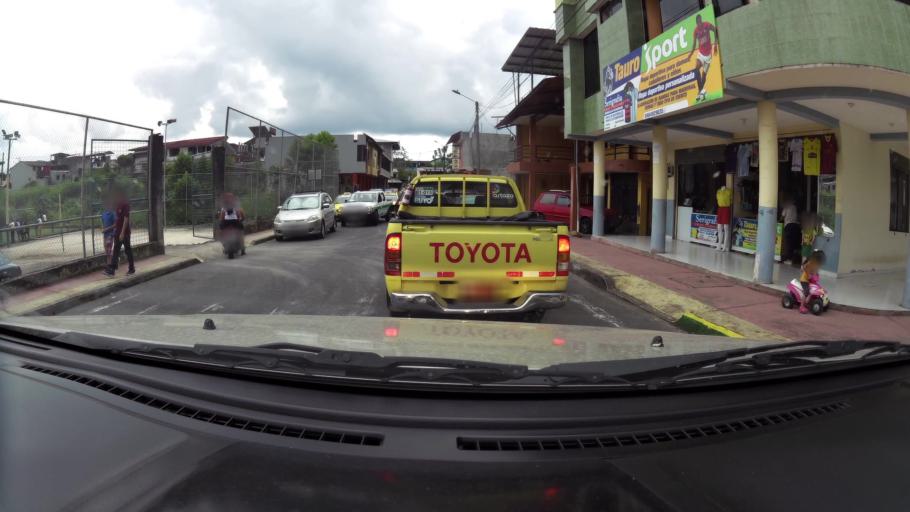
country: EC
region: Pastaza
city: Puyo
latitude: -1.4902
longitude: -78.0000
